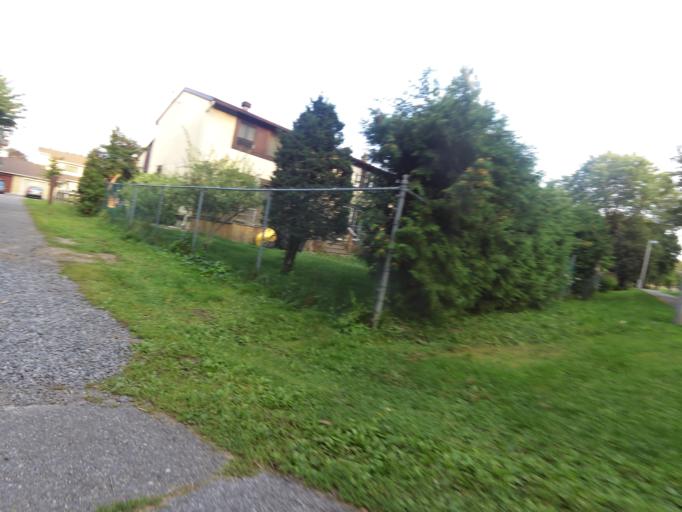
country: CA
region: Ontario
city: Bells Corners
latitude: 45.2774
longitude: -75.7588
